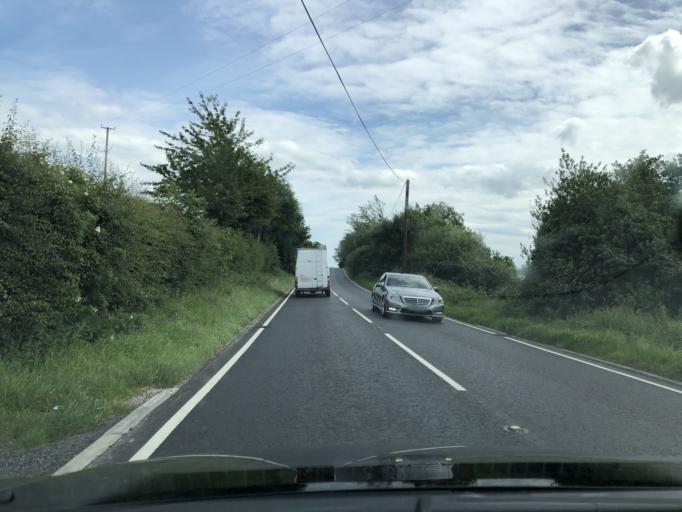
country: GB
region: Northern Ireland
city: Ballynahinch
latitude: 54.4335
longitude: -5.9328
